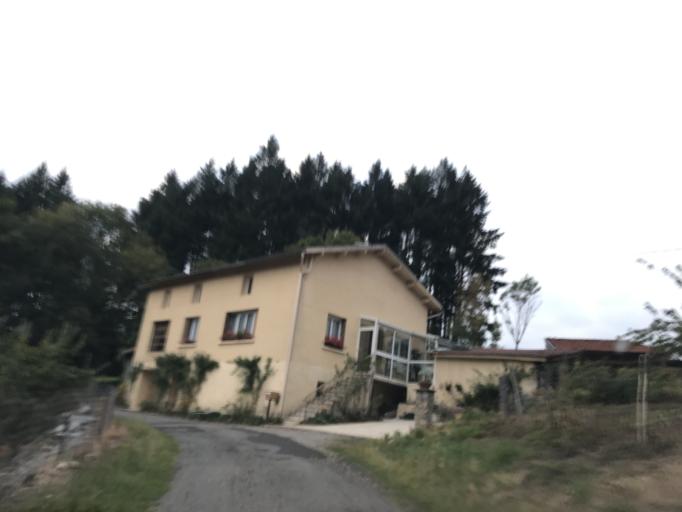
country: FR
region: Auvergne
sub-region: Departement du Puy-de-Dome
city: La Monnerie-le-Montel
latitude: 45.8513
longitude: 3.5930
